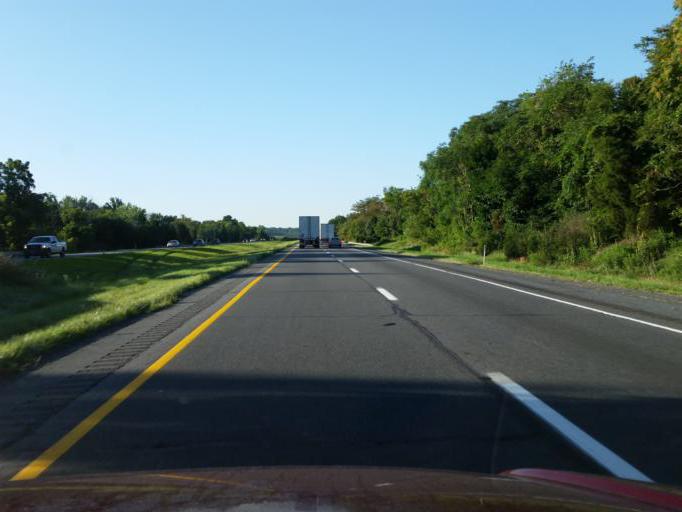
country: US
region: Pennsylvania
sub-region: Dauphin County
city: Middletown
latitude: 40.2139
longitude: -76.7088
